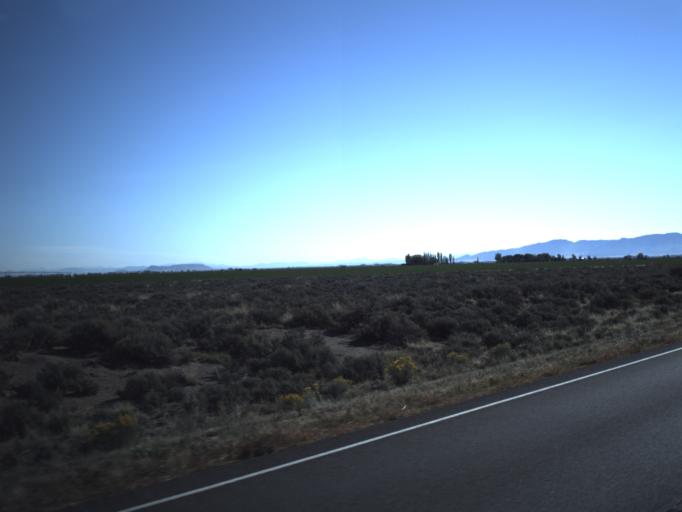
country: US
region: Utah
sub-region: Washington County
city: Enterprise
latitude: 37.7522
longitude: -113.7761
